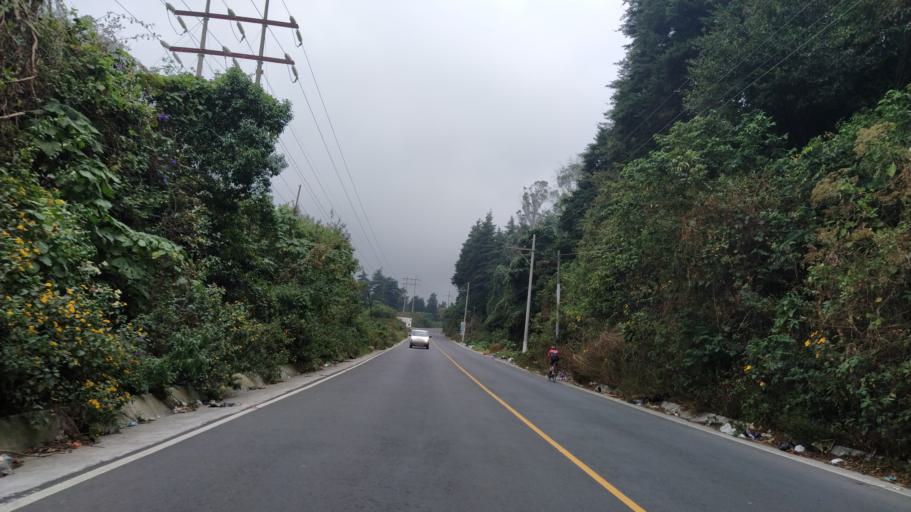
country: GT
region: Quetzaltenango
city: Zunil
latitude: 14.7417
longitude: -91.5159
